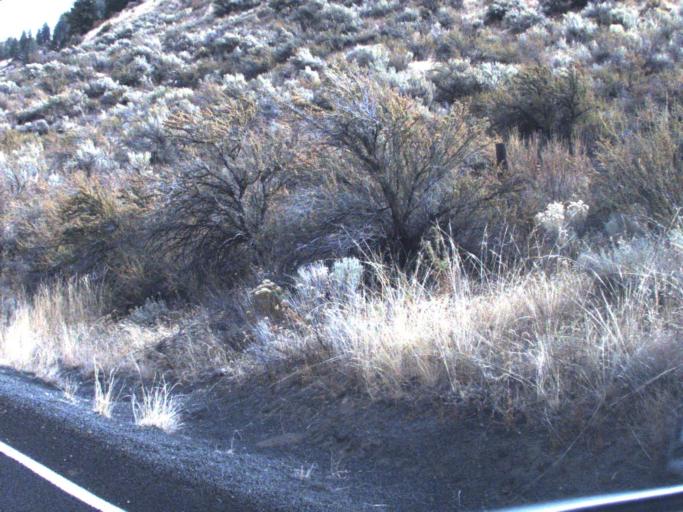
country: US
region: Washington
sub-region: Okanogan County
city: Coulee Dam
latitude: 47.8971
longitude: -118.7109
